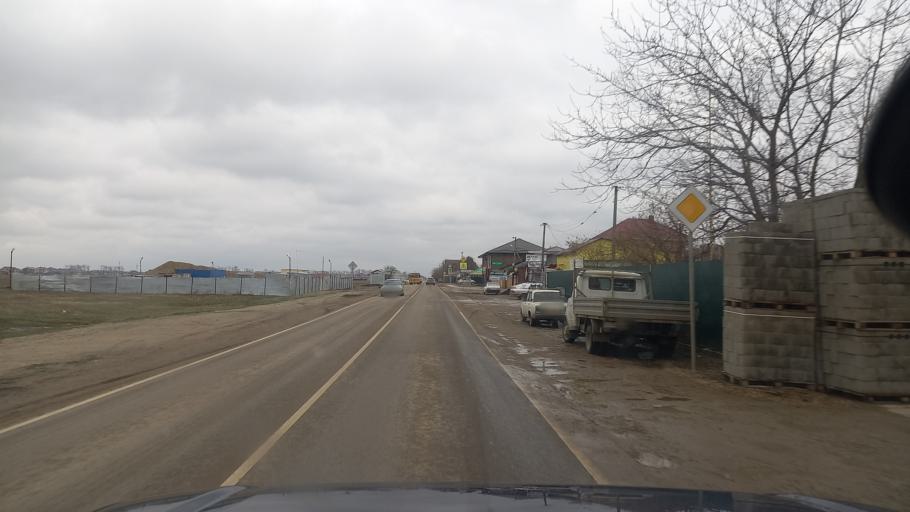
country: RU
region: Krasnodarskiy
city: Pashkovskiy
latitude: 45.0591
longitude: 39.1585
